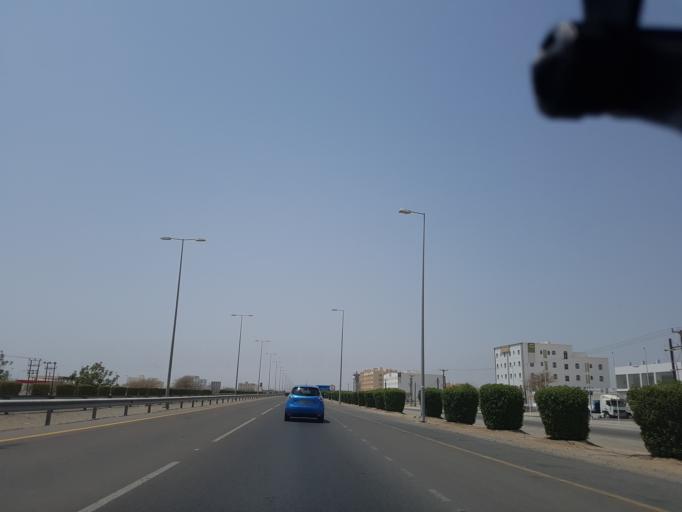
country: OM
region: Al Batinah
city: Al Liwa'
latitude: 24.4188
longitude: 56.6053
